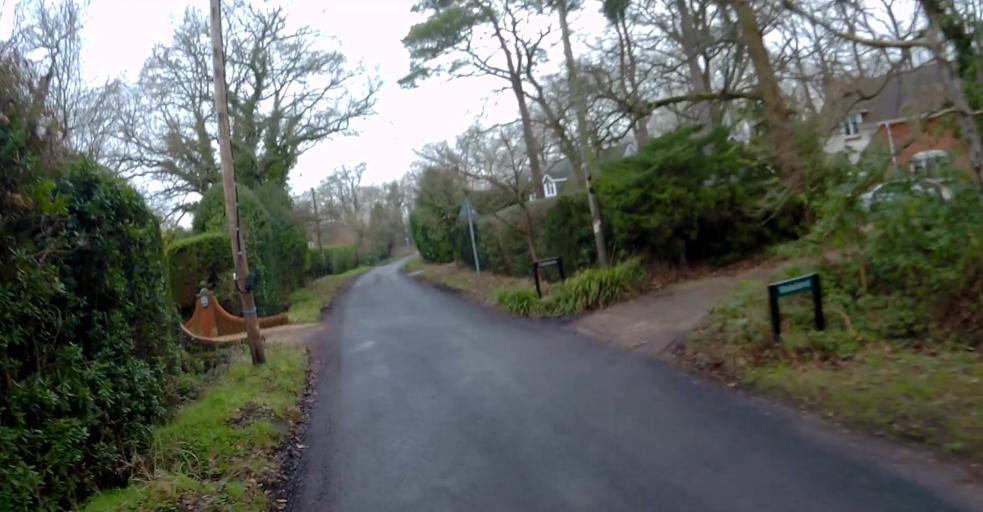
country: GB
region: England
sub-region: Hampshire
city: Eversley
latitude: 51.3582
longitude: -0.9069
